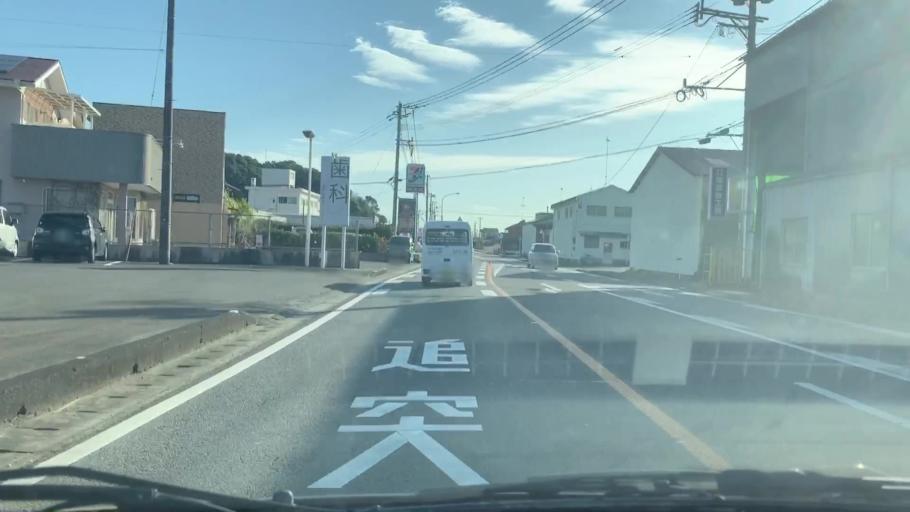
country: JP
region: Saga Prefecture
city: Takeocho-takeo
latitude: 33.2142
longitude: 130.0976
